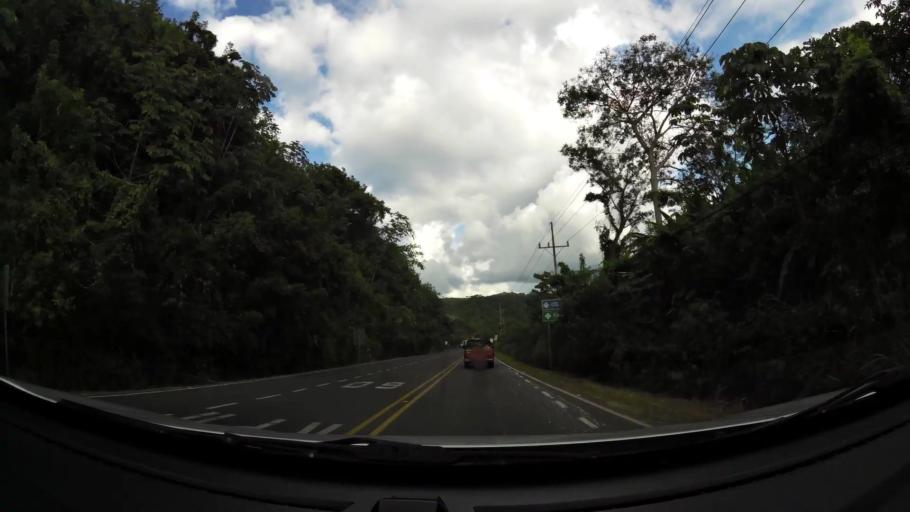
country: CR
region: Puntarenas
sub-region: Canton de Garabito
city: Jaco
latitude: 9.6887
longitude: -84.6458
